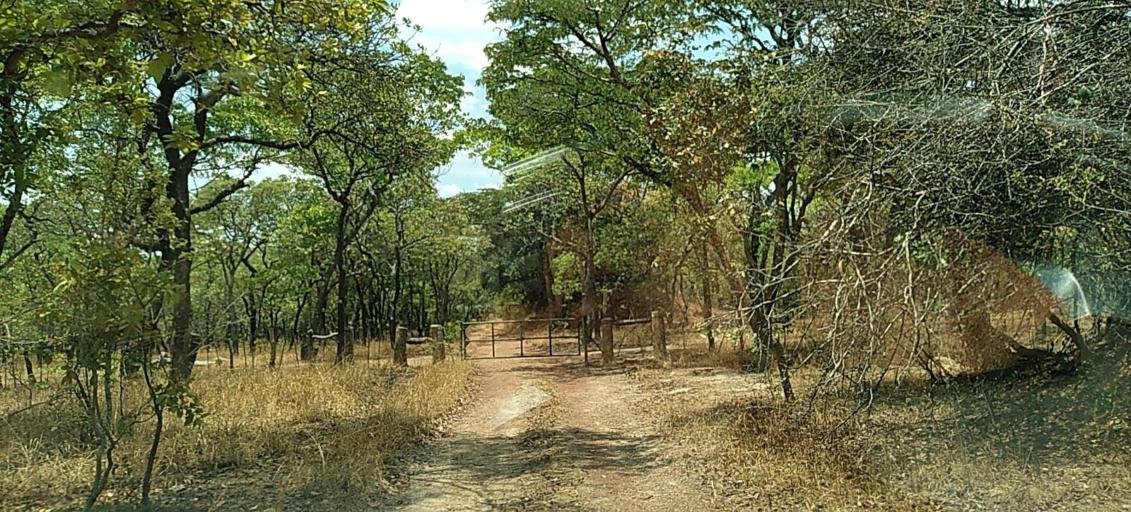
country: ZM
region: Copperbelt
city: Chililabombwe
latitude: -12.4580
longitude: 27.6984
